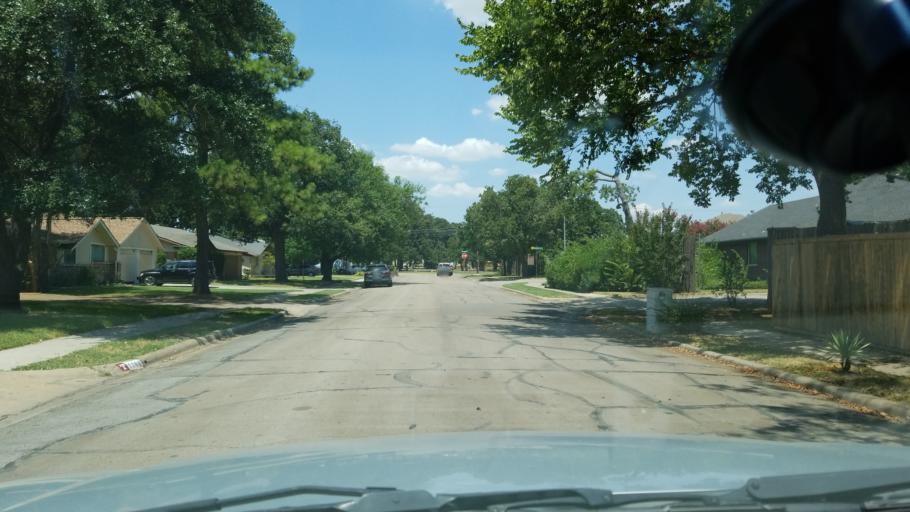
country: US
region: Texas
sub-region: Dallas County
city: Irving
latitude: 32.8274
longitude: -96.9893
